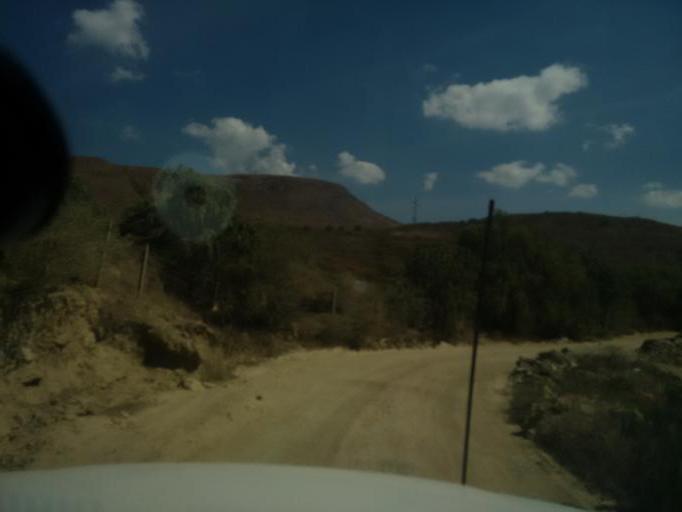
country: CO
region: Boyaca
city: Sachica
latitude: 5.5863
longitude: -73.5287
